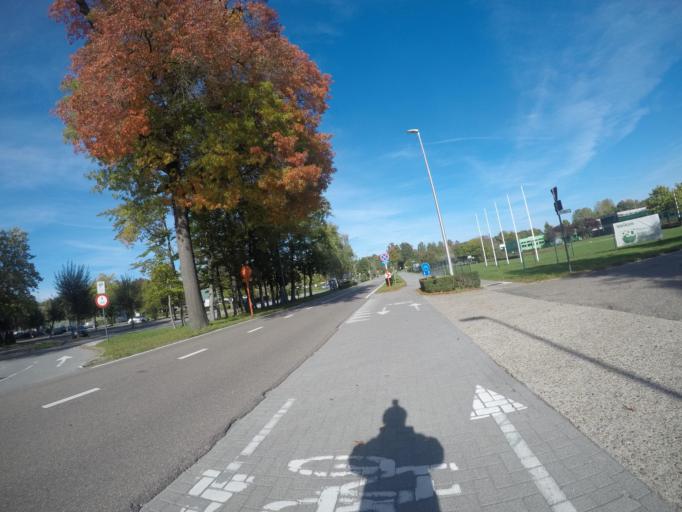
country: BE
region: Flanders
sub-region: Provincie Limburg
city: Diepenbeek
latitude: 50.9126
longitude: 5.4219
